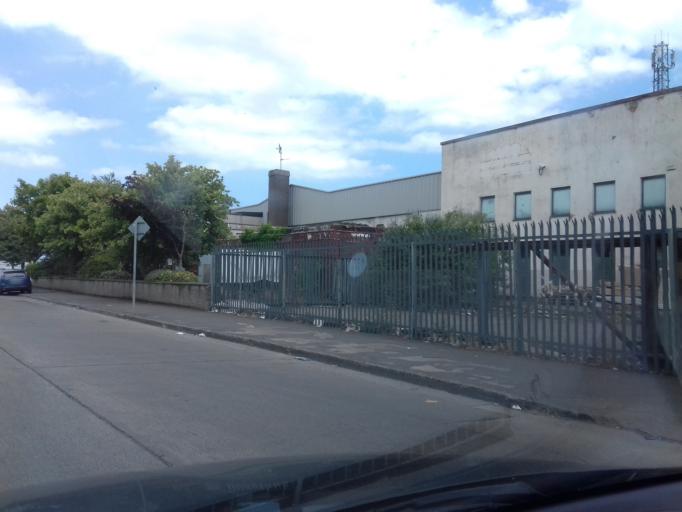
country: IE
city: Coolock
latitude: 53.3935
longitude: -6.1971
